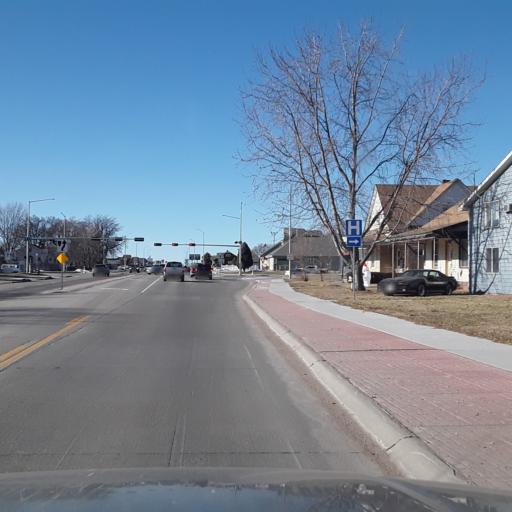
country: US
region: Nebraska
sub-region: Phelps County
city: Holdrege
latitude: 40.4380
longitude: -99.3783
